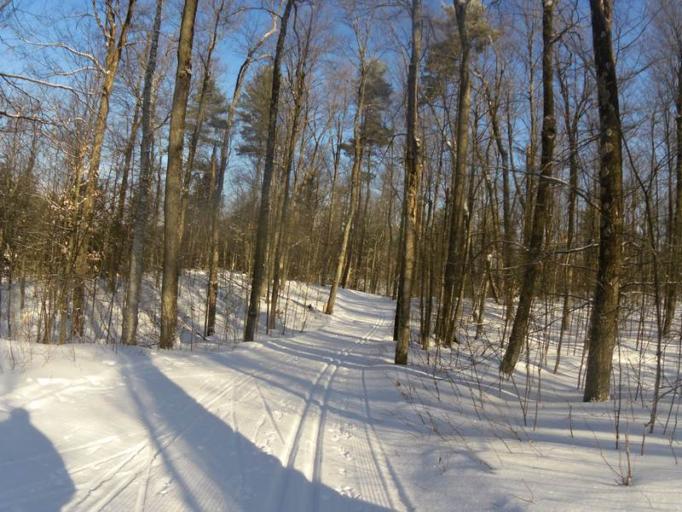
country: CA
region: Quebec
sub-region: Outaouais
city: Wakefield
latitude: 45.5272
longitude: -75.9289
